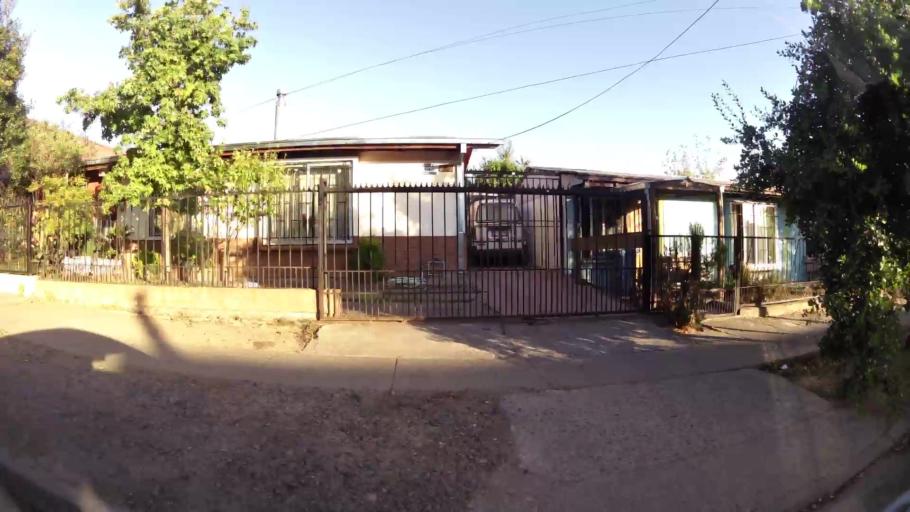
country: CL
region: Maule
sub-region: Provincia de Talca
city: Talca
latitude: -35.4397
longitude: -71.6441
